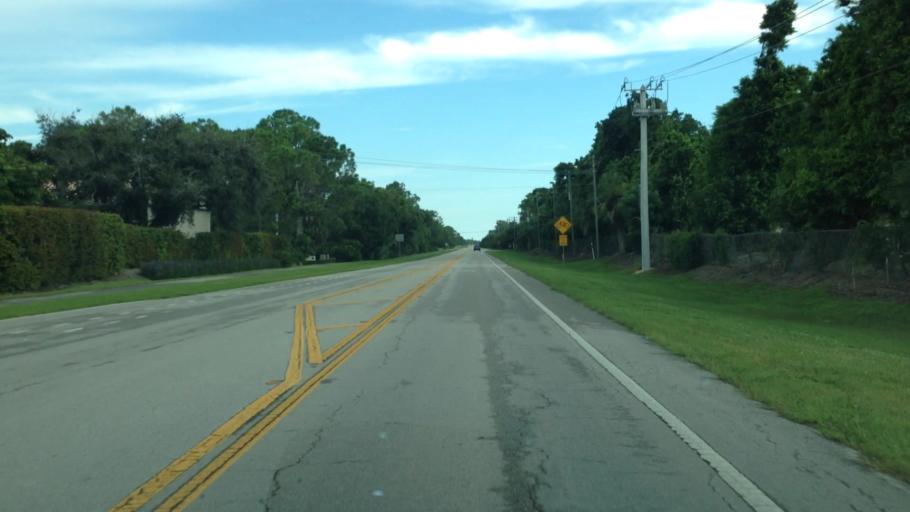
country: US
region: Florida
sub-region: Collier County
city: Naples Park
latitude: 26.3060
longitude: -81.8188
